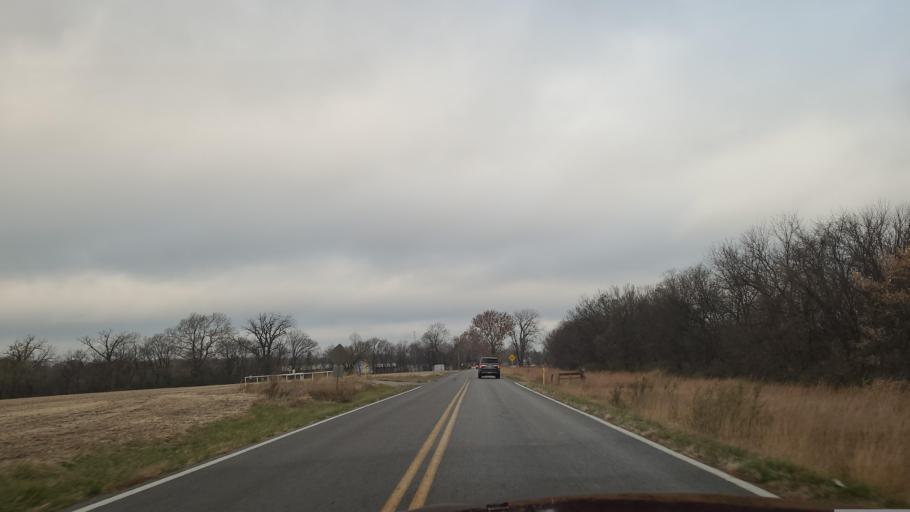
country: US
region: Kansas
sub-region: Douglas County
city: Lawrence
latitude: 38.9630
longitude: -95.2015
